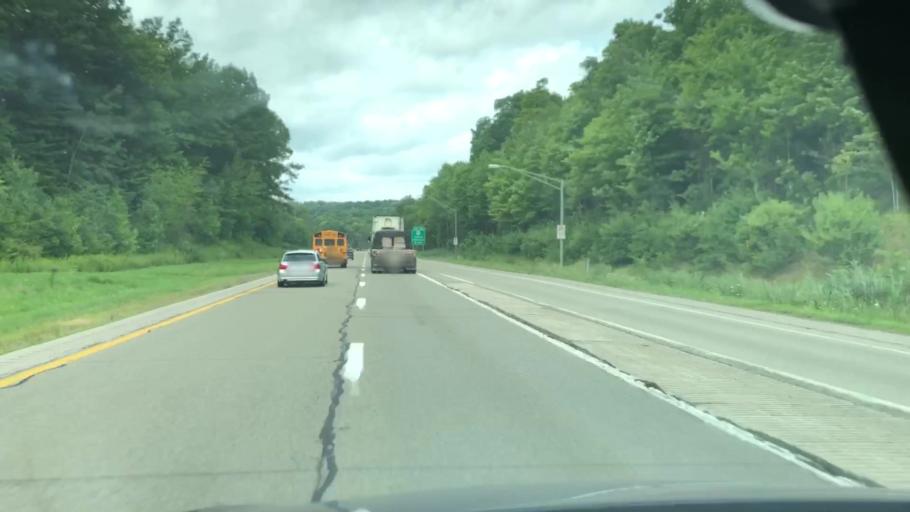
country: US
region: Pennsylvania
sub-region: Erie County
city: Edinboro
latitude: 41.8454
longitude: -80.1753
